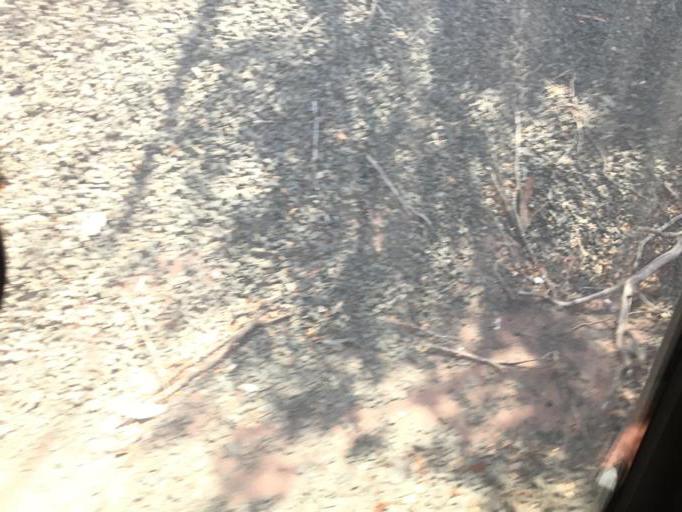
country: US
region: Connecticut
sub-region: New Haven County
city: Meriden
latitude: 41.5073
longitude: -72.8154
